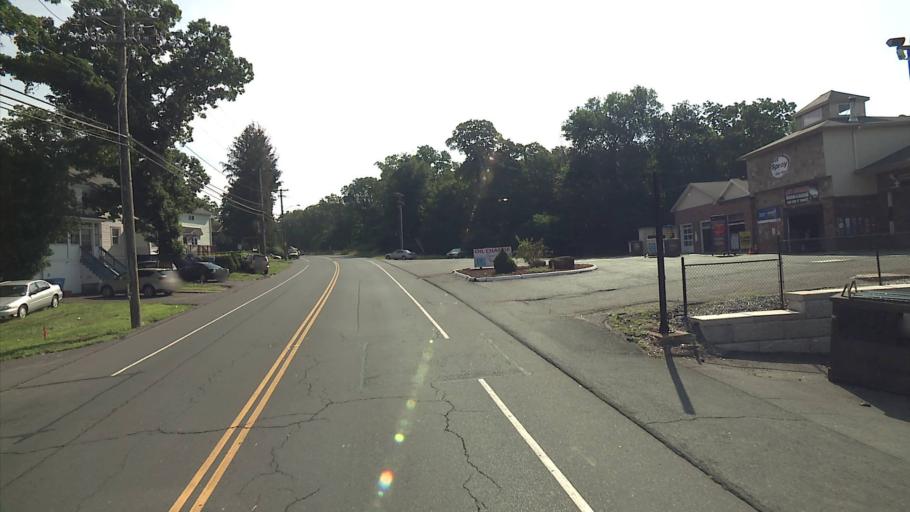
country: US
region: Connecticut
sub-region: New Haven County
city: Wolcott
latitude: 41.5530
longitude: -72.9985
